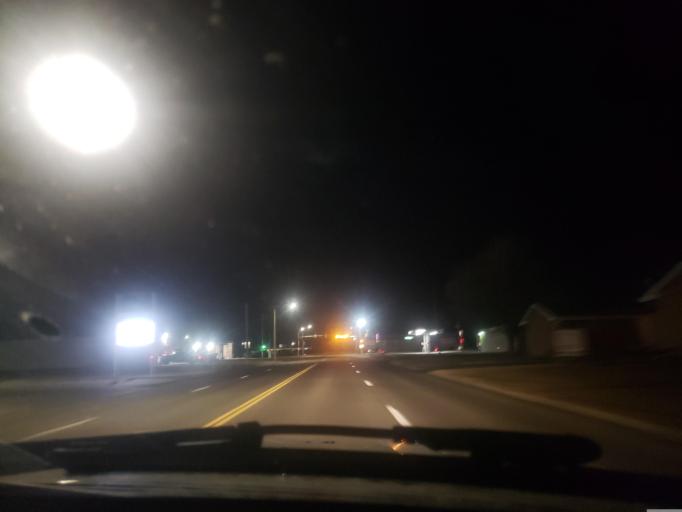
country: US
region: Kansas
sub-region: Finney County
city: Garden City
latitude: 37.9658
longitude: -100.8544
